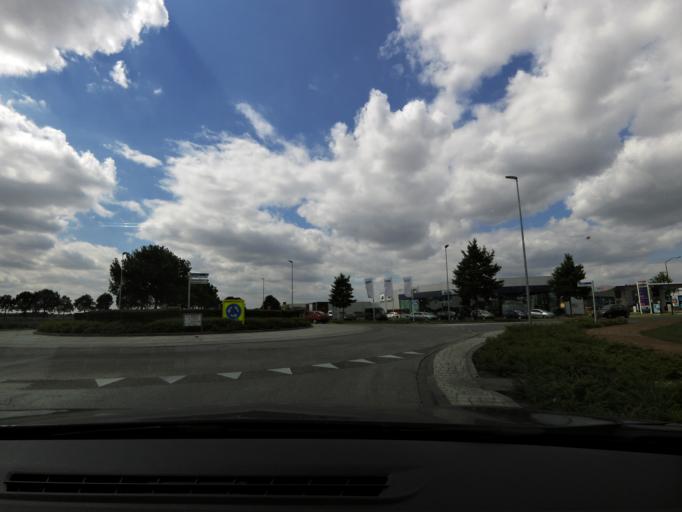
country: NL
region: North Brabant
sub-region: Gemeente Dongen
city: Dongen
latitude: 51.6127
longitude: 4.9353
